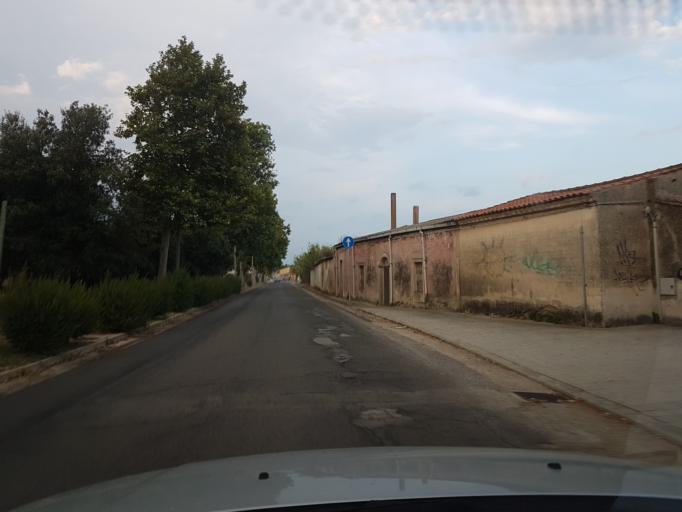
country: IT
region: Sardinia
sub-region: Provincia di Oristano
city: Solanas
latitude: 39.9301
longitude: 8.5492
